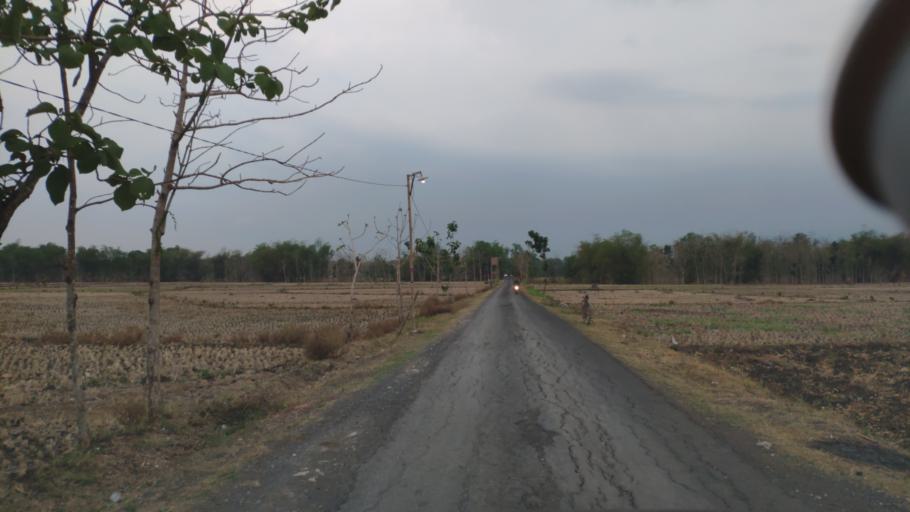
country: ID
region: Central Java
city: Kalangan
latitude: -6.9471
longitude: 111.3749
